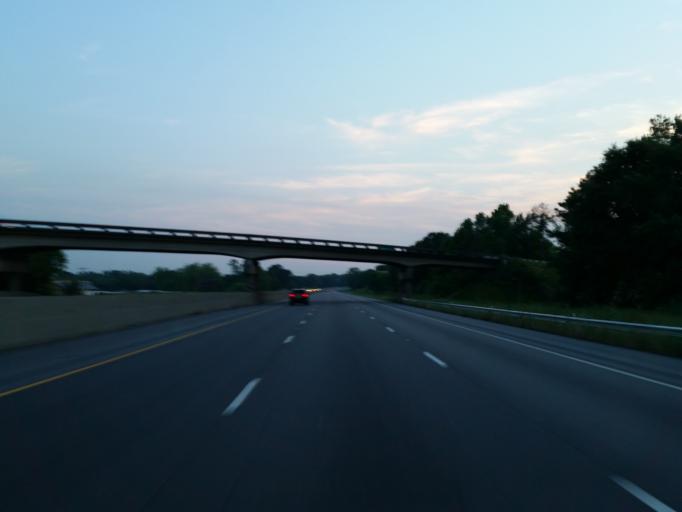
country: US
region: Alabama
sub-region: Calhoun County
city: Oxford
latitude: 33.5907
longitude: -85.8654
